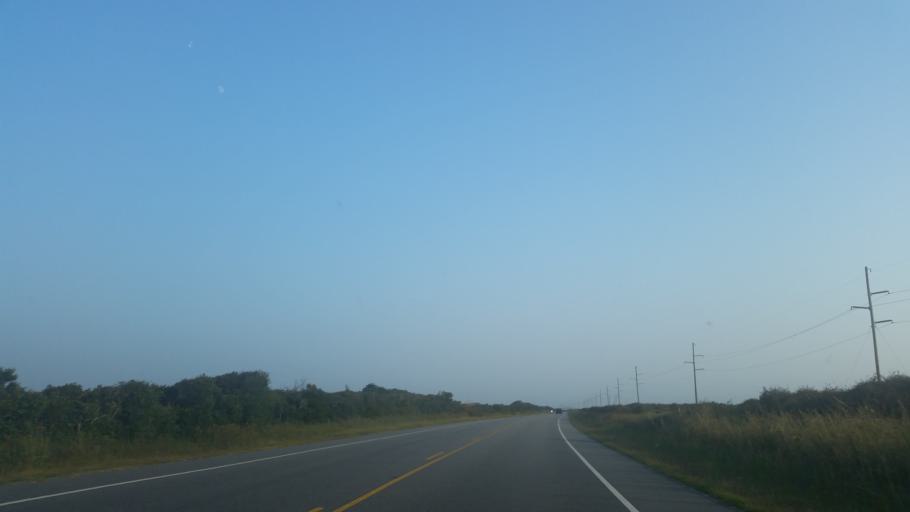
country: US
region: North Carolina
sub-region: Dare County
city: Wanchese
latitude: 35.8201
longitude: -75.5538
